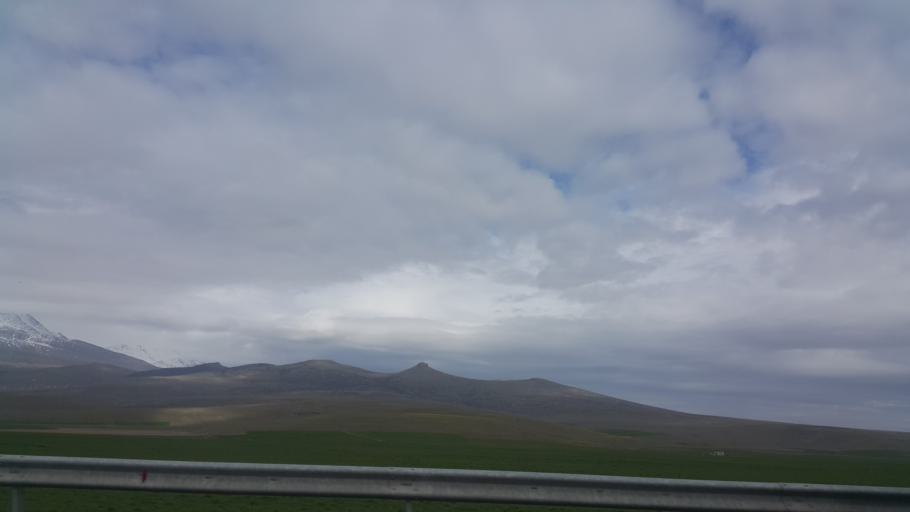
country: TR
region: Aksaray
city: Taspinar
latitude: 38.0614
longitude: 34.0323
